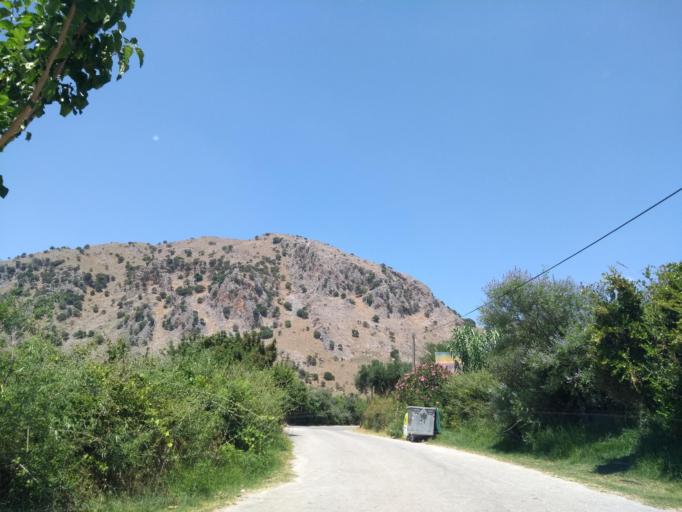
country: GR
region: Crete
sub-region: Nomos Chanias
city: Georgioupolis
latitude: 35.3334
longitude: 24.2787
